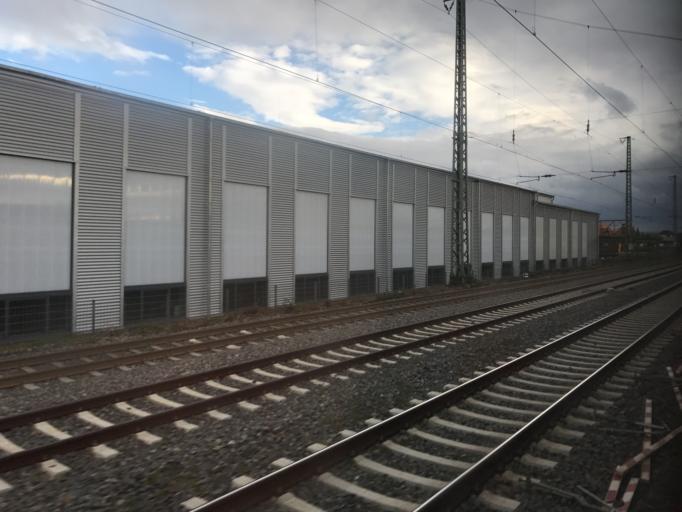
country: DE
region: North Rhine-Westphalia
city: Witten
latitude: 51.4438
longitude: 7.3256
